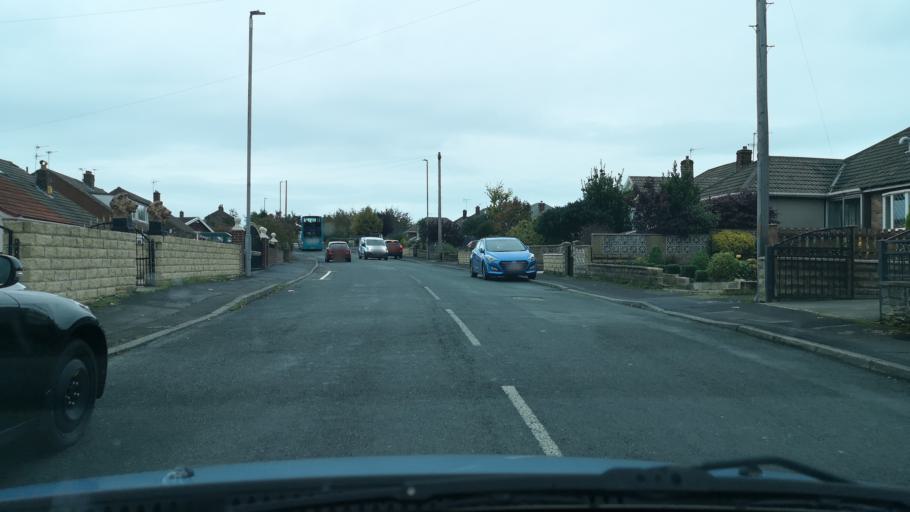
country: GB
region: England
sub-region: Kirklees
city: Heckmondwike
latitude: 53.7184
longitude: -1.6707
